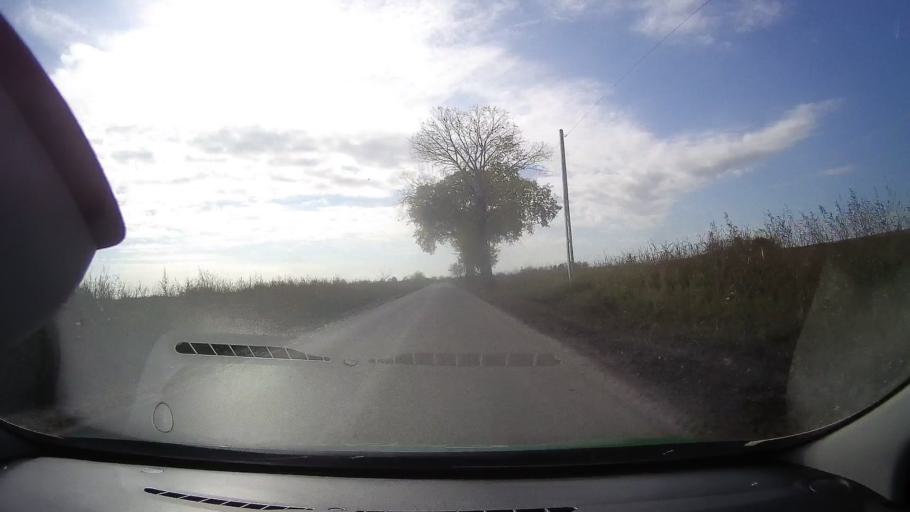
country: RO
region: Tulcea
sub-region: Comuna Valea Nucarilor
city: Agighiol
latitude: 44.9853
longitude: 28.8842
